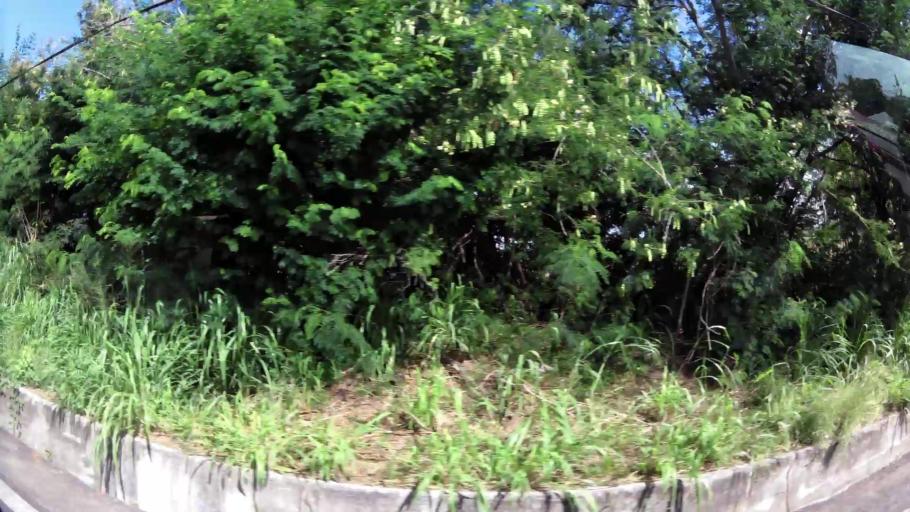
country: GP
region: Guadeloupe
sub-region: Guadeloupe
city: Vieux-Habitants
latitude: 16.0542
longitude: -61.7637
